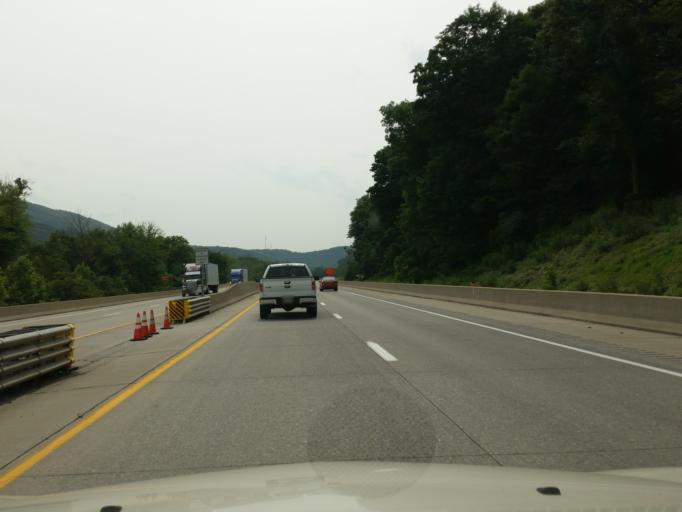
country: US
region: Pennsylvania
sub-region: Mifflin County
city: Lewistown
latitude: 40.5854
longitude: -77.5251
